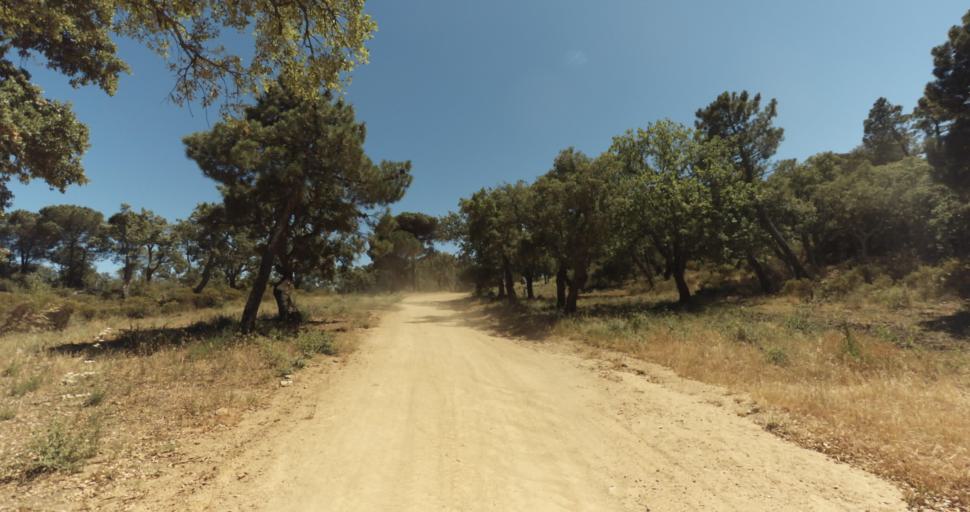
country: FR
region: Provence-Alpes-Cote d'Azur
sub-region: Departement du Var
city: Gassin
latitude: 43.2523
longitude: 6.5644
